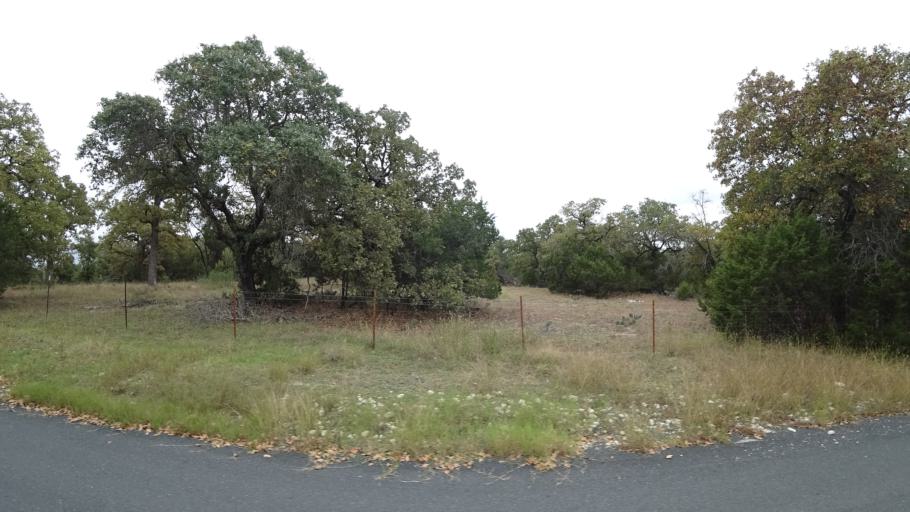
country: US
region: Texas
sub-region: Travis County
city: Bee Cave
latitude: 30.3442
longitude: -97.9323
